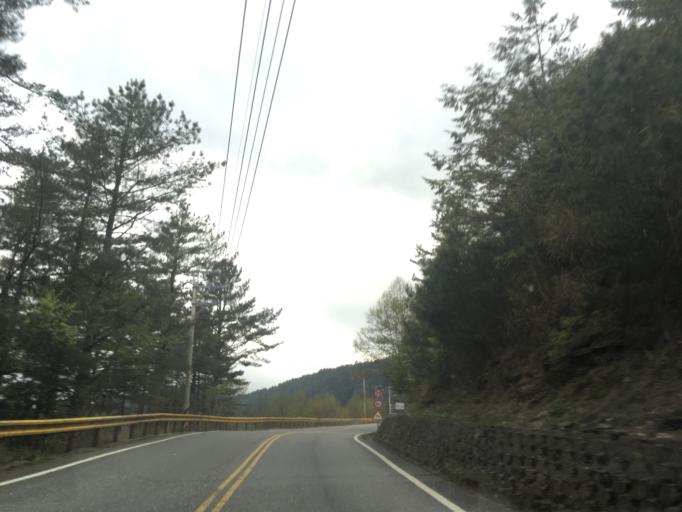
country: TW
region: Taiwan
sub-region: Hualien
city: Hualian
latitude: 24.1803
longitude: 121.3091
